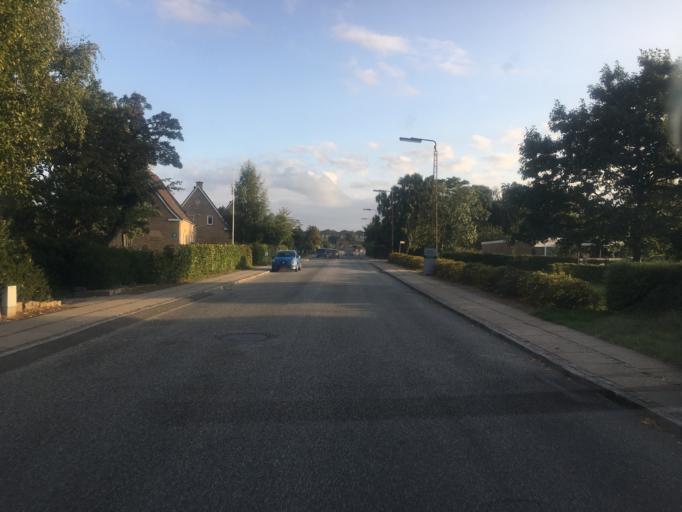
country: DK
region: South Denmark
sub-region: Tonder Kommune
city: Tonder
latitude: 54.9459
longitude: 8.8791
